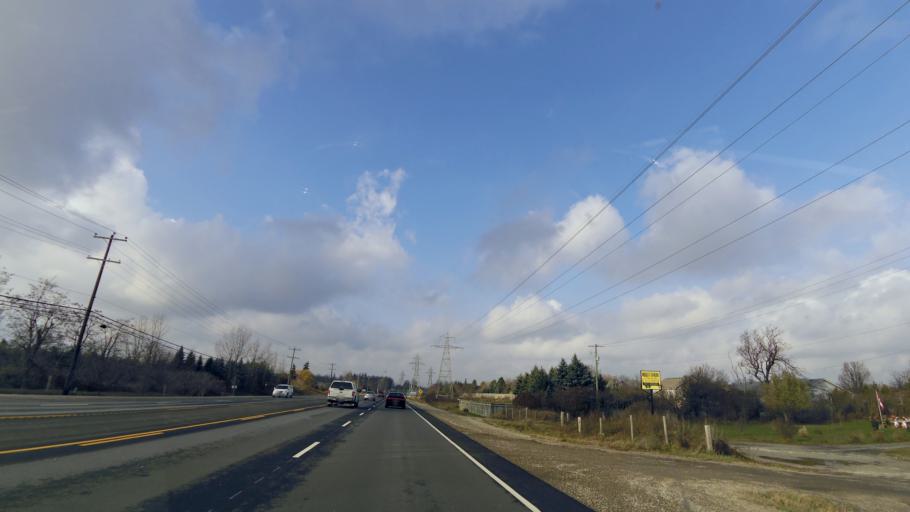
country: CA
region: Ontario
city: Ancaster
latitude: 43.3922
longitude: -80.0264
